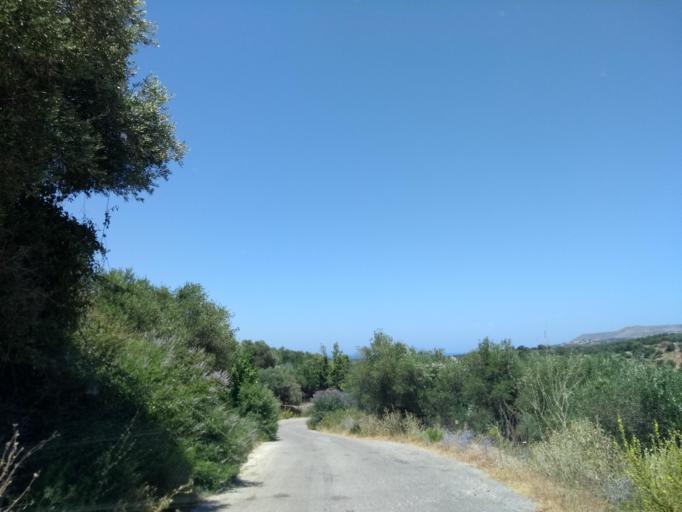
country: GR
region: Crete
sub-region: Nomos Chanias
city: Georgioupolis
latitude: 35.3208
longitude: 24.3125
